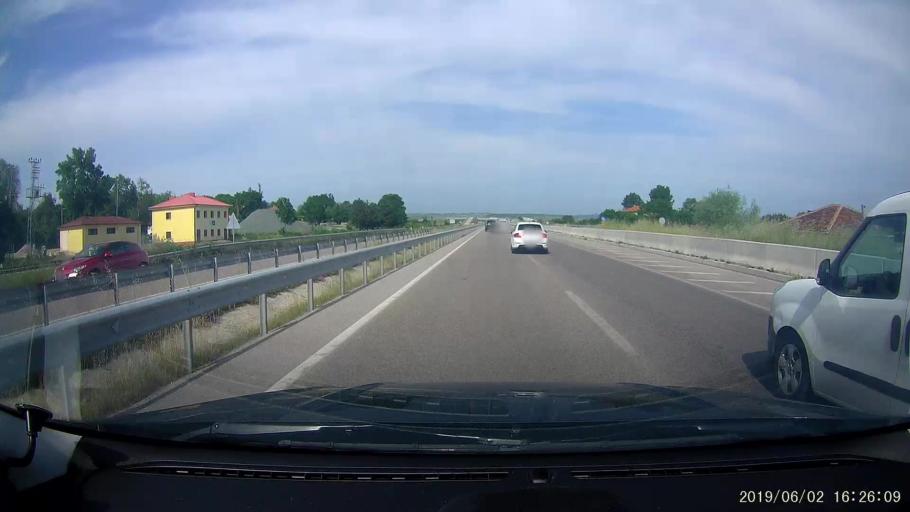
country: TR
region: Samsun
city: Ladik
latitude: 40.9981
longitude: 35.7946
